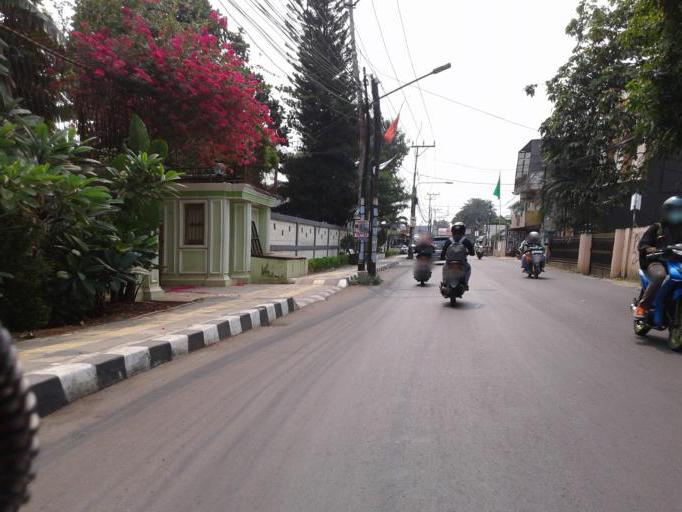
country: ID
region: Banten
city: South Tangerang
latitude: -6.3043
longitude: 106.7563
